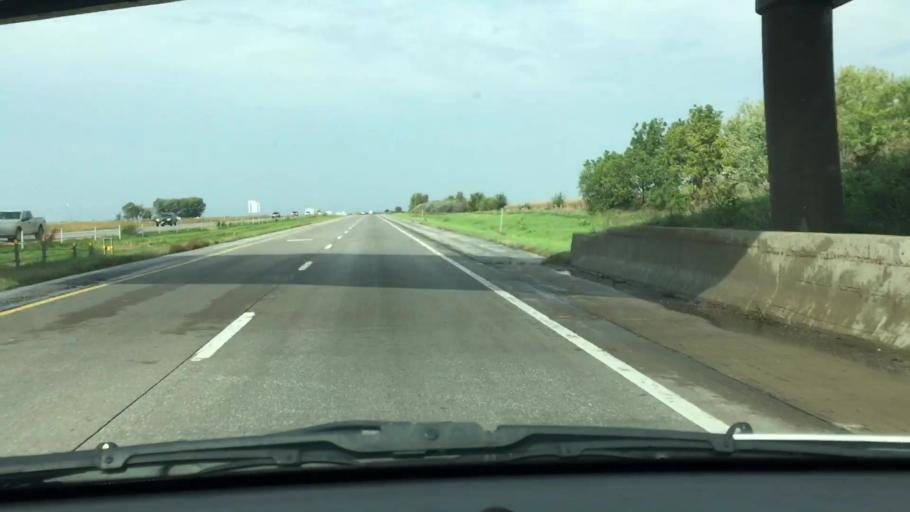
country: US
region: Iowa
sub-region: Scott County
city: Walcott
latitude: 41.6250
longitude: -90.8134
